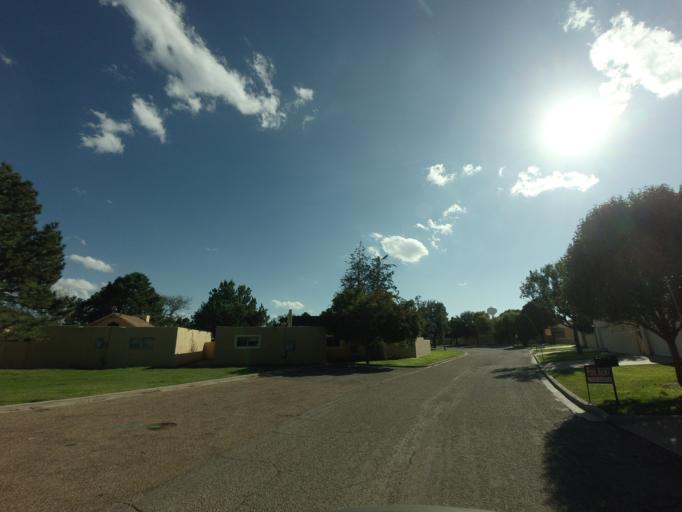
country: US
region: New Mexico
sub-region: Curry County
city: Clovis
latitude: 34.4354
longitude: -103.1832
